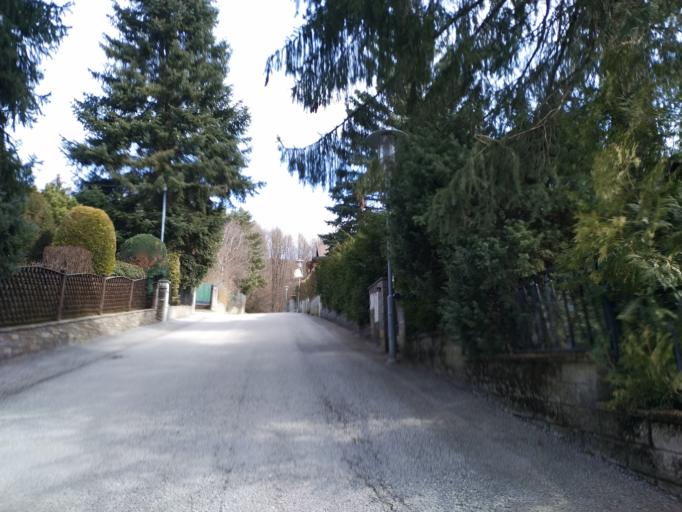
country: AT
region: Lower Austria
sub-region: Politischer Bezirk Wien-Umgebung
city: Gablitz
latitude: 48.2293
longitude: 16.1613
